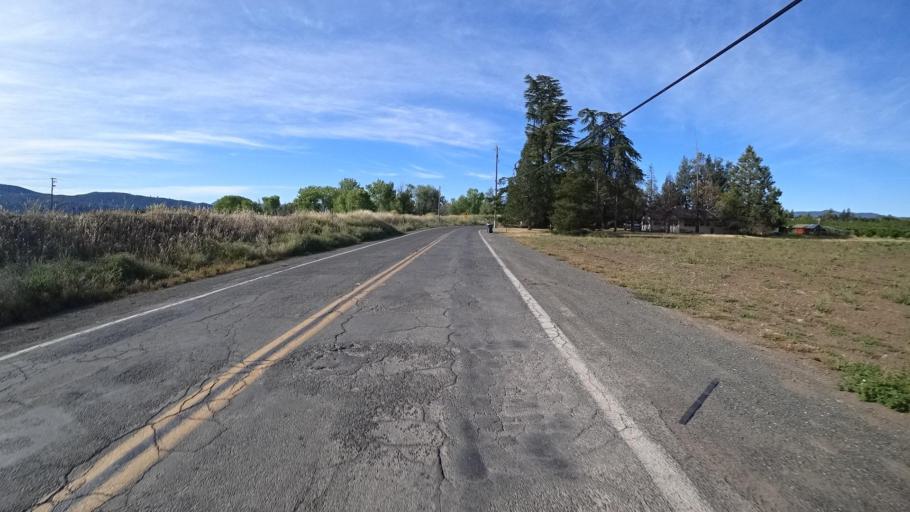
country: US
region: California
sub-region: Lake County
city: Kelseyville
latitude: 38.9873
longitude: -122.8461
